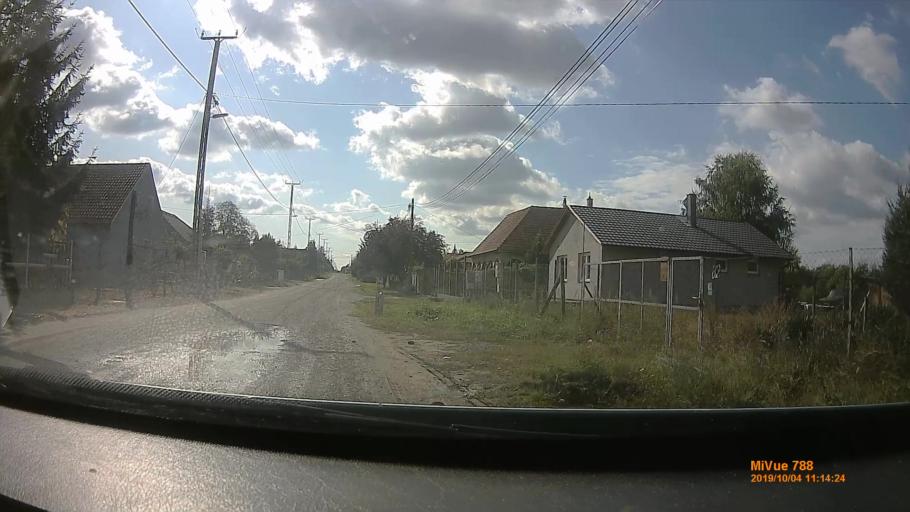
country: HU
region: Szabolcs-Szatmar-Bereg
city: Nyirtelek
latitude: 47.9943
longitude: 21.6759
